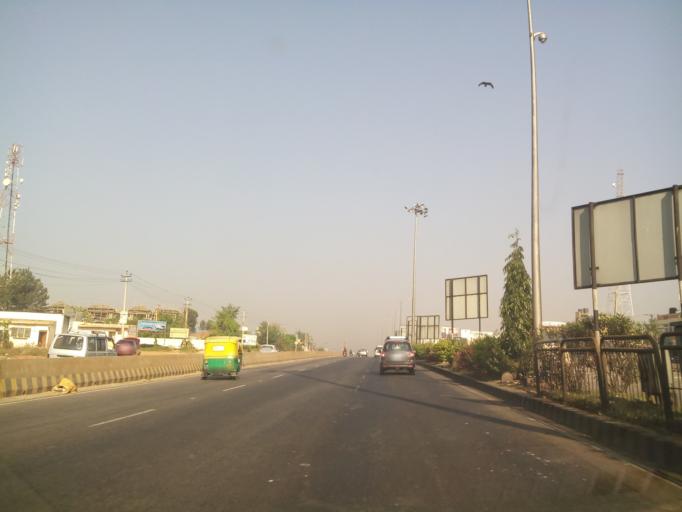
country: IN
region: Karnataka
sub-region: Bangalore Rural
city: Nelamangala
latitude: 13.0908
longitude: 77.3997
